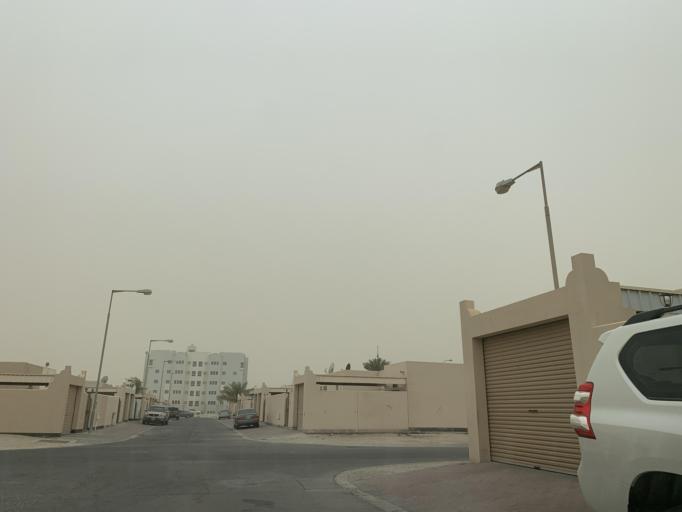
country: BH
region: Central Governorate
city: Madinat Hamad
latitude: 26.1328
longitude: 50.5250
